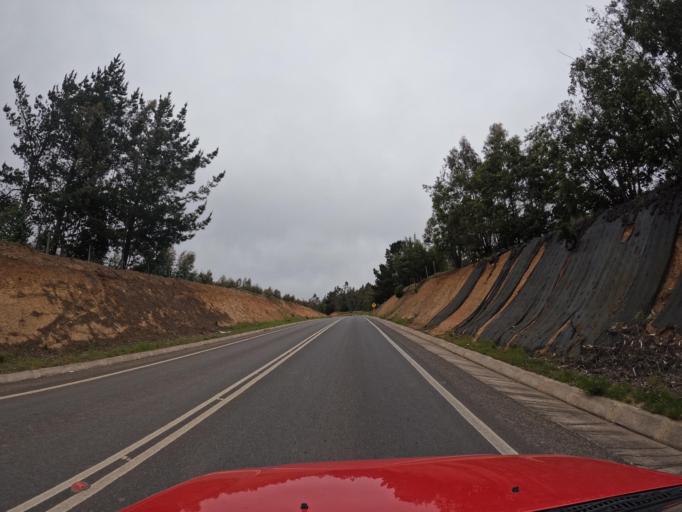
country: CL
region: O'Higgins
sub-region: Provincia de Colchagua
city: Santa Cruz
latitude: -34.6139
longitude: -72.0123
